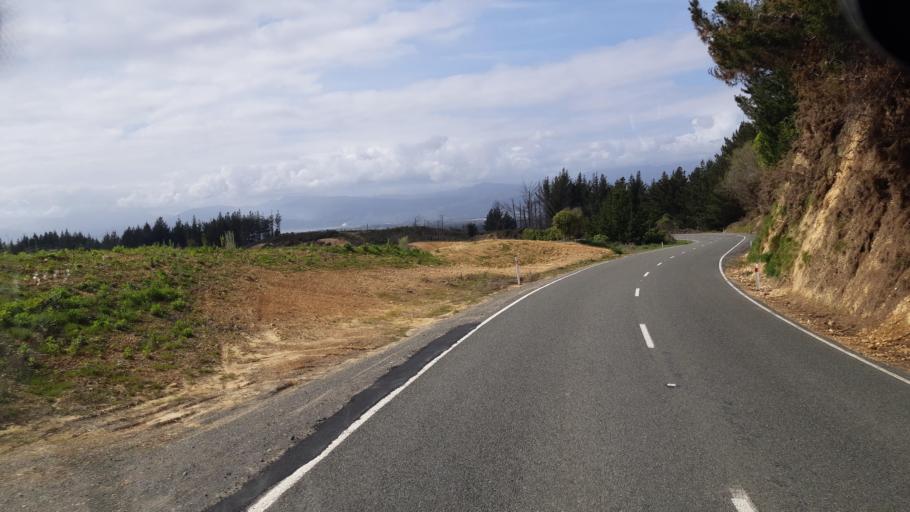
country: NZ
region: Tasman
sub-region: Tasman District
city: Mapua
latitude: -41.2991
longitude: 173.0454
